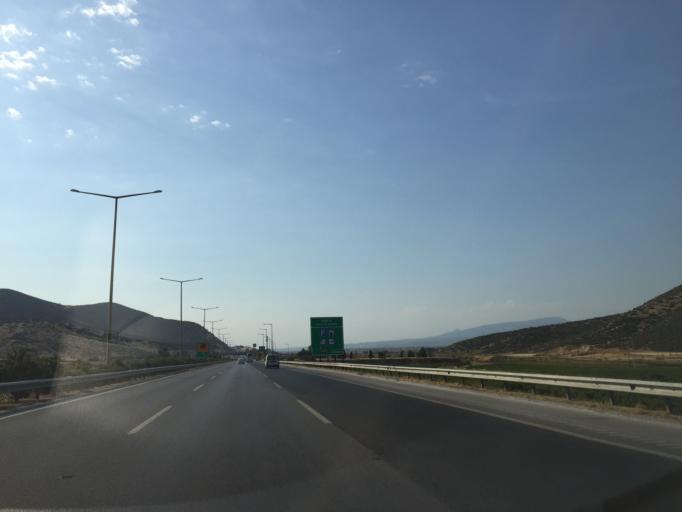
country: TR
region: Izmir
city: Belevi
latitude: 38.0640
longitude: 27.4172
